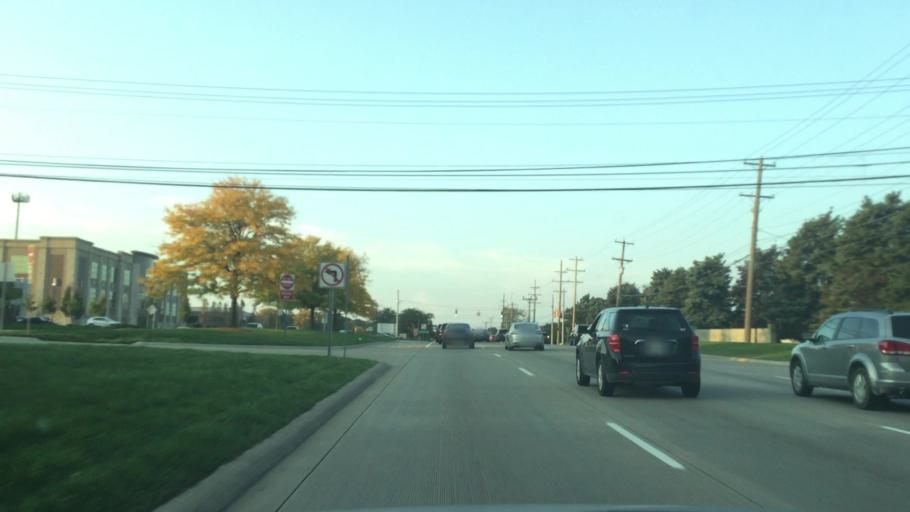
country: US
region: Michigan
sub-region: Oakland County
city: Bloomfield Hills
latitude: 42.5782
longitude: -83.2807
